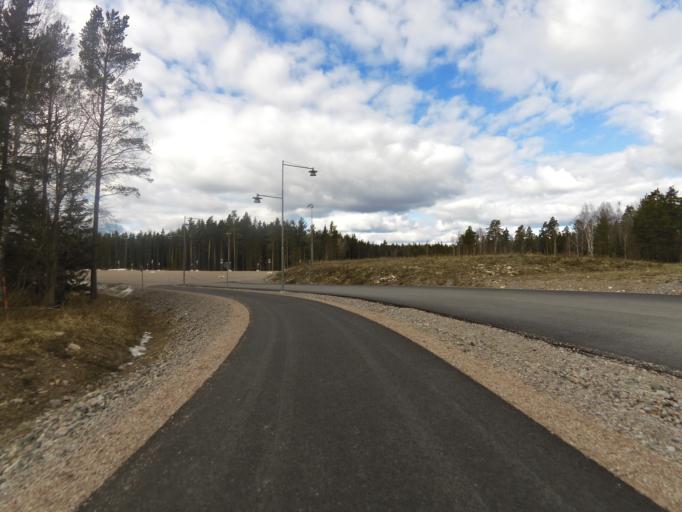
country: SE
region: Gaevleborg
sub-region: Gavle Kommun
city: Gavle
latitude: 60.6940
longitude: 17.1328
